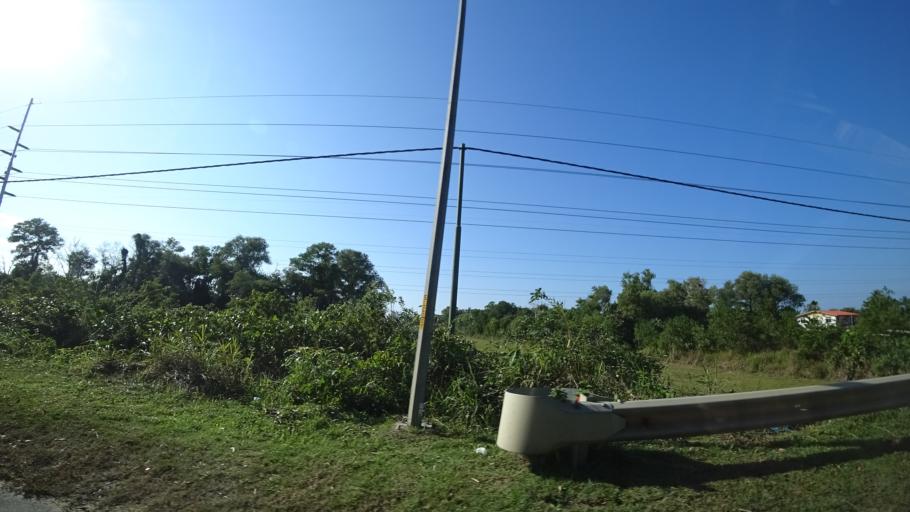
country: BN
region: Tutong
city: Tutong
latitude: 4.7246
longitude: 114.5494
